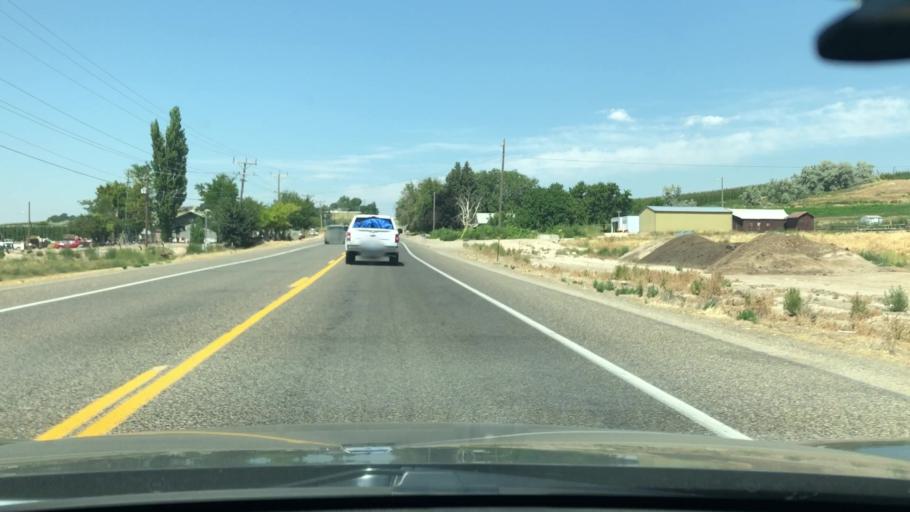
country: US
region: Idaho
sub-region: Canyon County
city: Wilder
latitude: 43.6531
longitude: -116.9120
